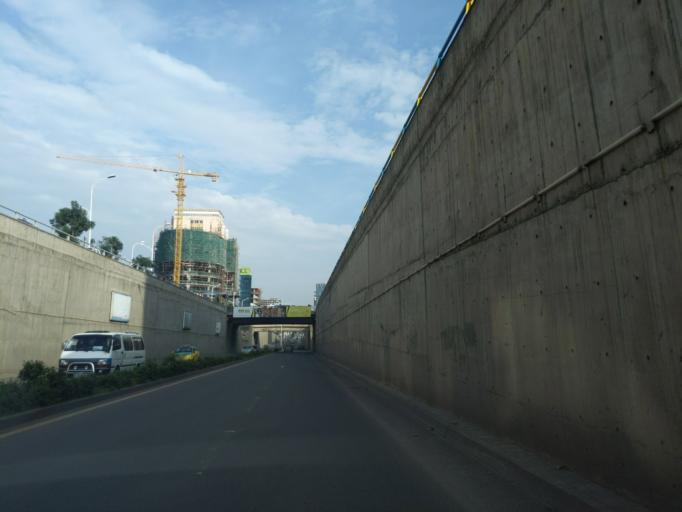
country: ET
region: Adis Abeba
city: Addis Ababa
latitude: 9.0053
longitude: 38.7675
